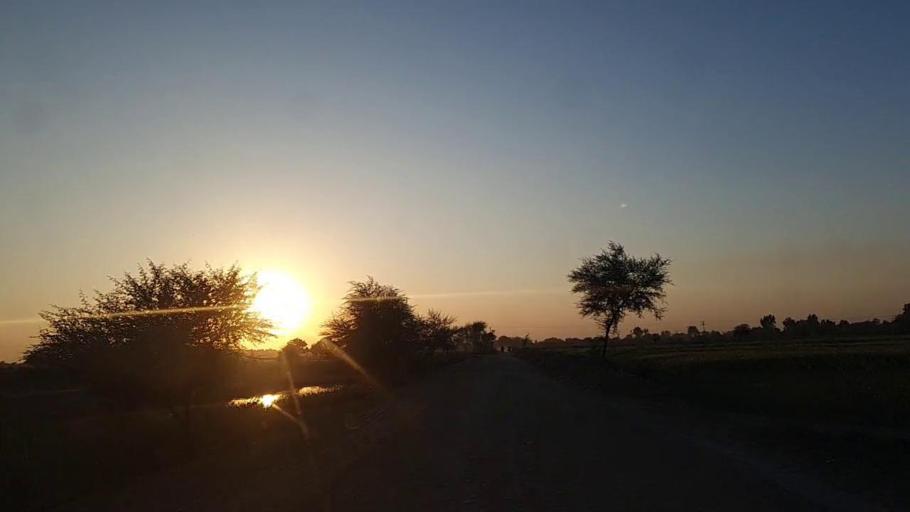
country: PK
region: Sindh
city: Naukot
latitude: 25.0563
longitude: 69.4043
